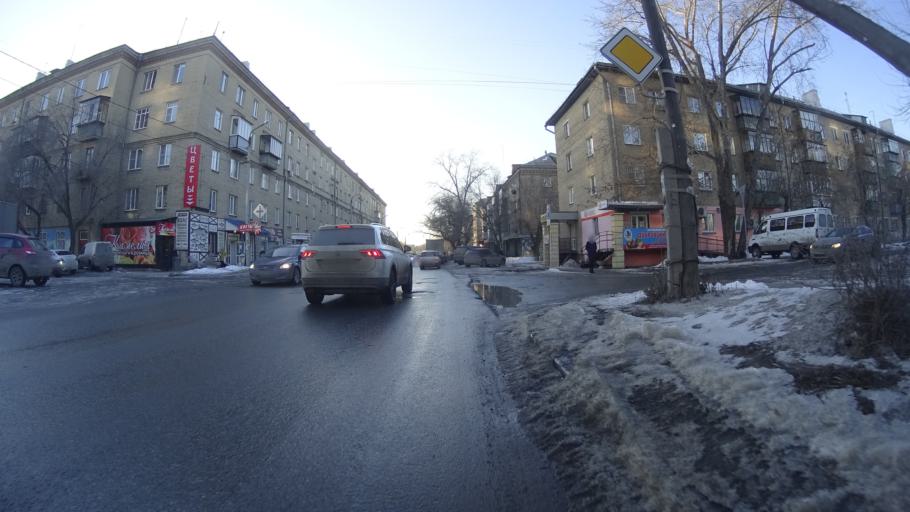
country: RU
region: Chelyabinsk
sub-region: Gorod Chelyabinsk
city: Chelyabinsk
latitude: 55.1388
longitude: 61.4432
